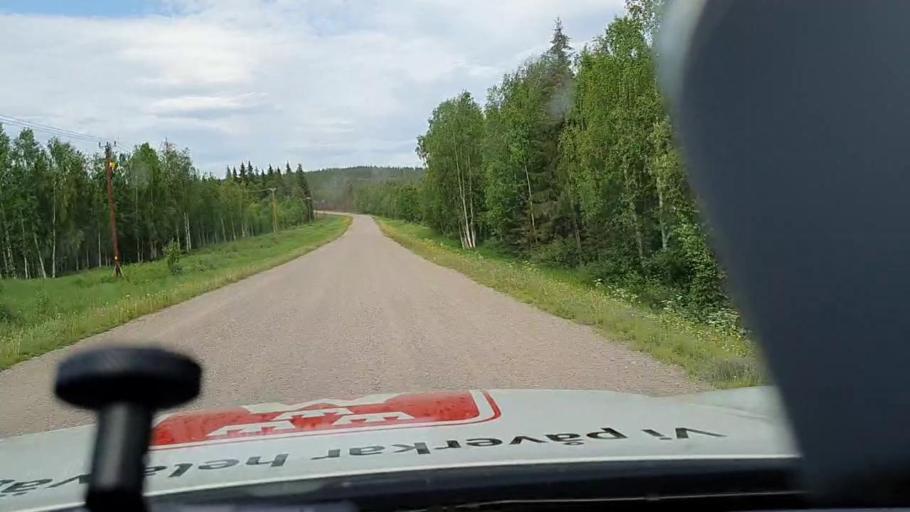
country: SE
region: Norrbotten
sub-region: Alvsbyns Kommun
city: AElvsbyn
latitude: 66.1194
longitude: 20.9830
